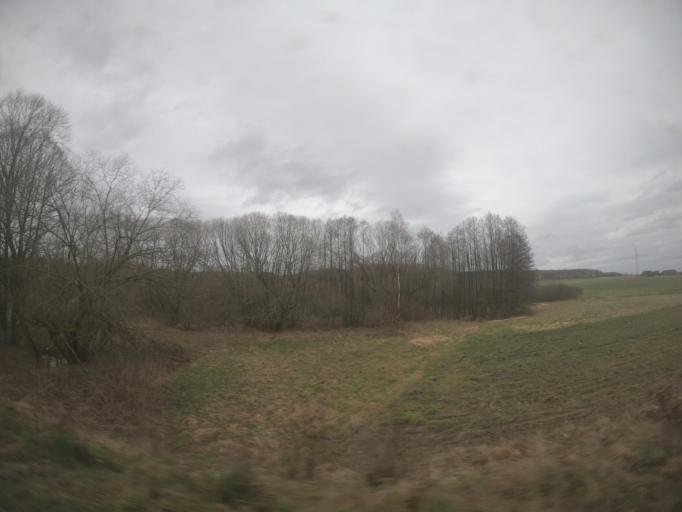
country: PL
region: West Pomeranian Voivodeship
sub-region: Powiat szczecinecki
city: Szczecinek
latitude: 53.7199
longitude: 16.7868
